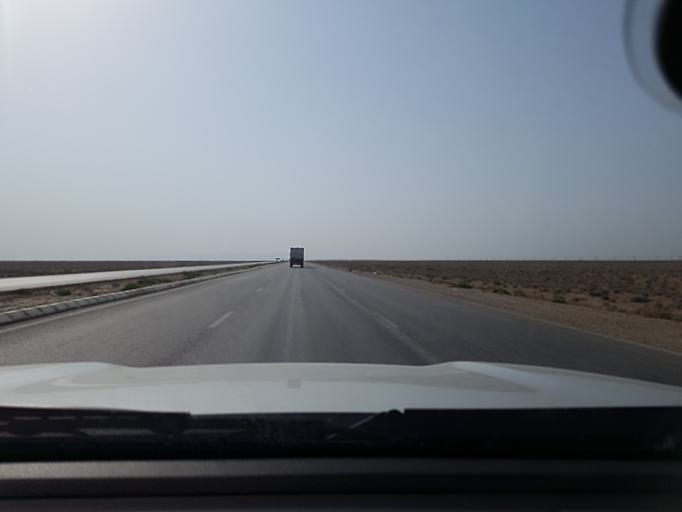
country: TM
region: Balkan
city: Balkanabat
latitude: 39.4720
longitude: 54.4241
